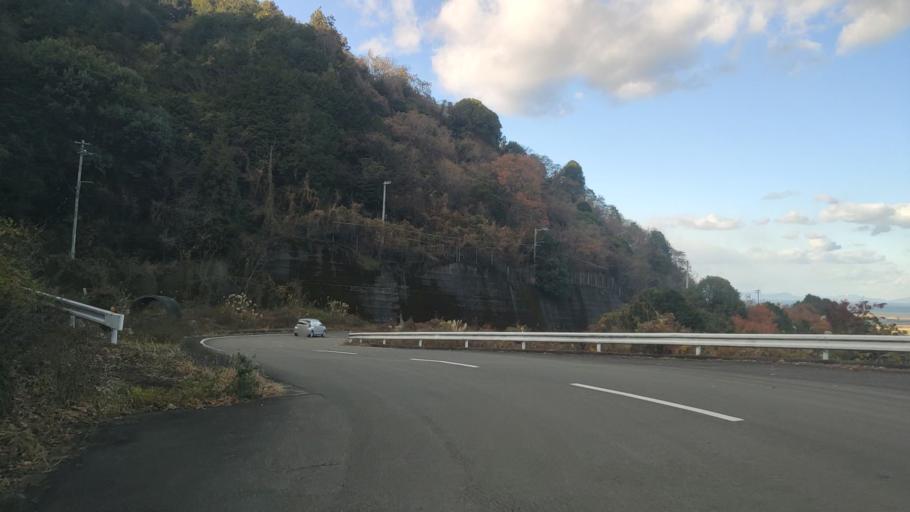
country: JP
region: Ehime
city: Saijo
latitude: 33.8810
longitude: 133.1328
